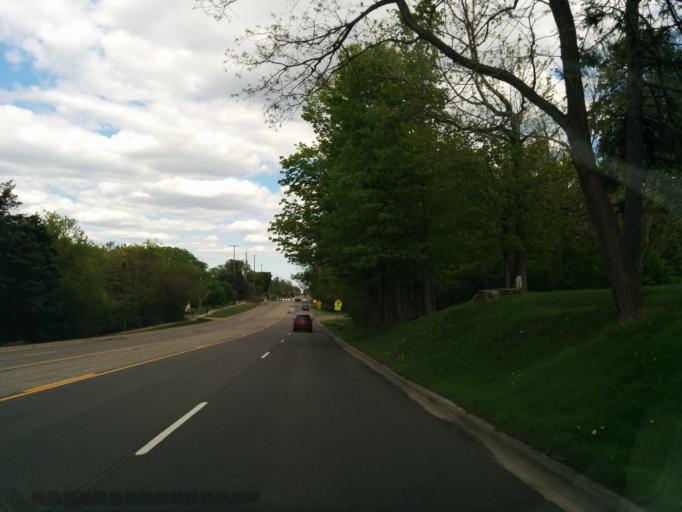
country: US
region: Michigan
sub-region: Oakland County
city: Farmington Hills
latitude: 42.4994
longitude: -83.3519
